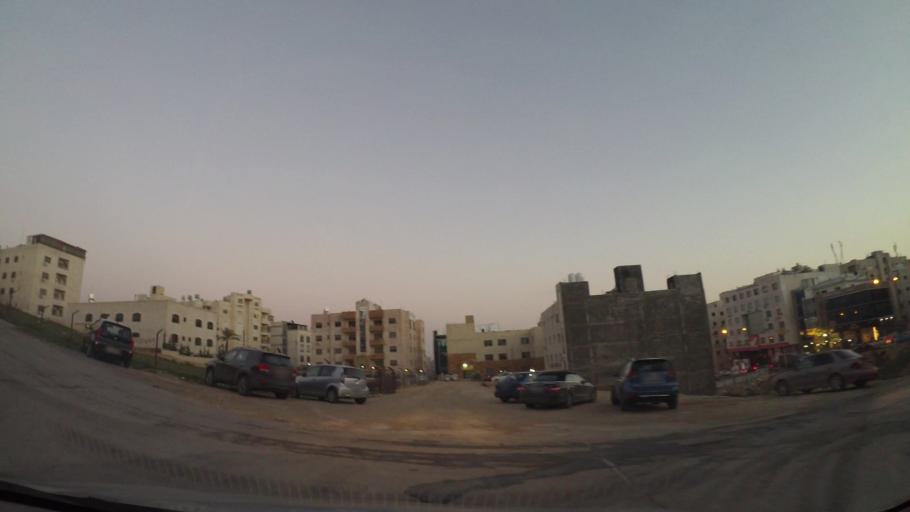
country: JO
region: Amman
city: Al Jubayhah
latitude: 31.9966
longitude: 35.8559
